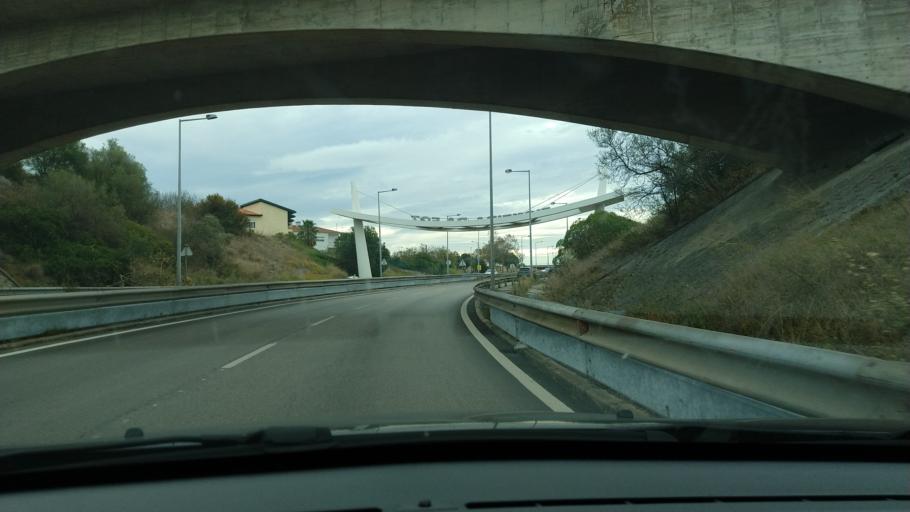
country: PT
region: Coimbra
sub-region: Figueira da Foz
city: Figueira da Foz
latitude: 40.1527
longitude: -8.8456
